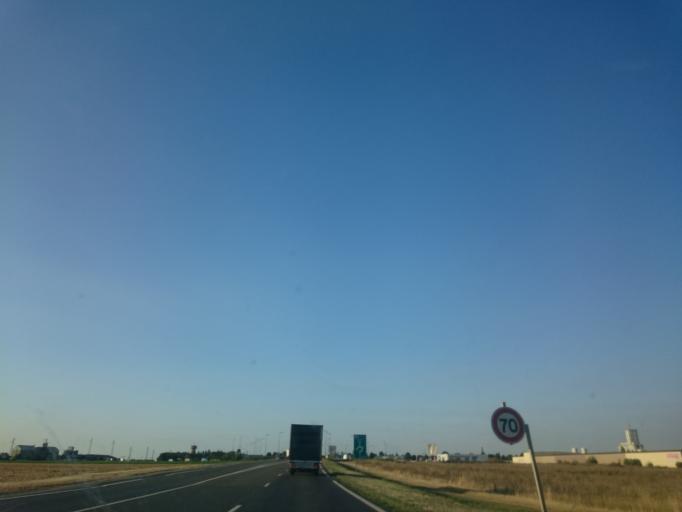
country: FR
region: Centre
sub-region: Departement d'Eure-et-Loir
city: Toury
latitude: 48.1809
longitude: 1.9272
